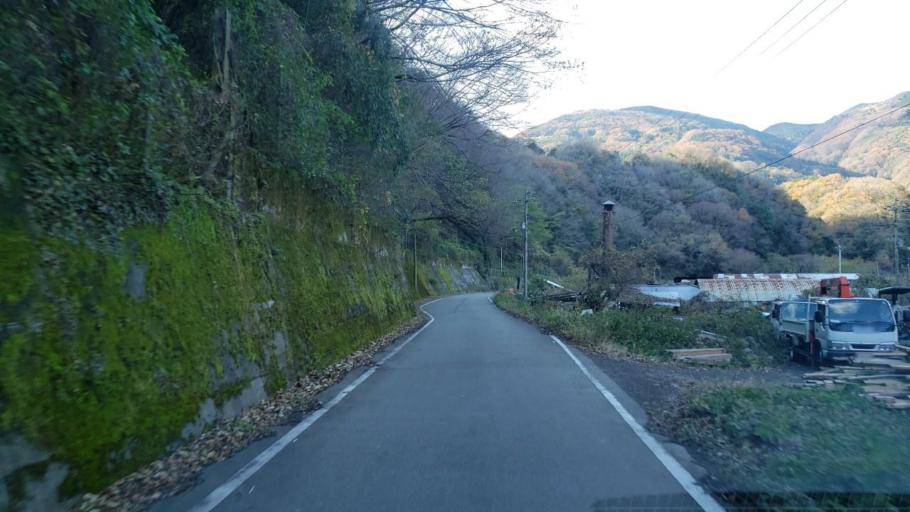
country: JP
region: Tokushima
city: Wakimachi
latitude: 34.0886
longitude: 134.0697
